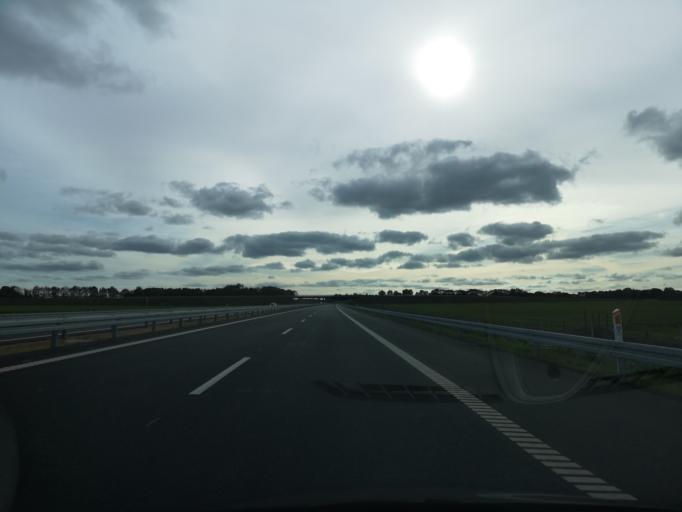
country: DK
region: Central Jutland
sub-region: Herning Kommune
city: Avlum
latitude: 56.3208
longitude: 8.7323
